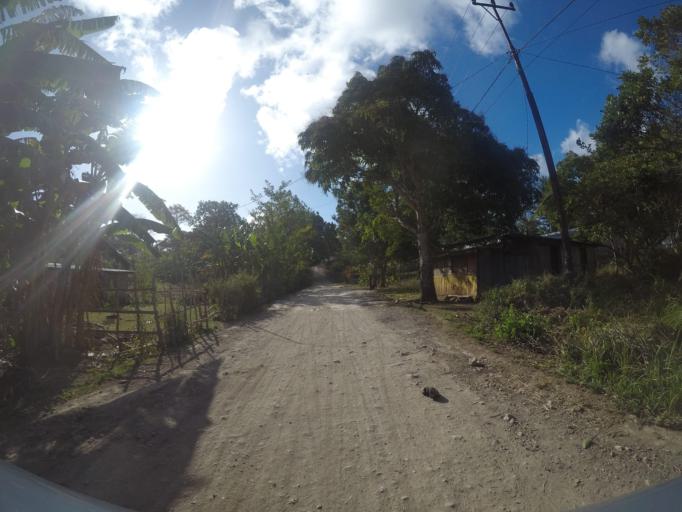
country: TL
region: Lautem
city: Lospalos
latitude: -8.4535
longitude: 126.8845
